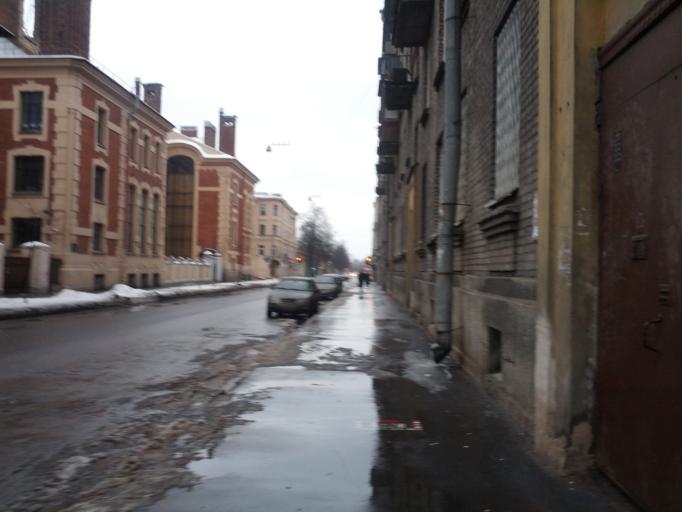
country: RU
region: St.-Petersburg
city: Centralniy
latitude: 59.9093
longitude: 30.3497
